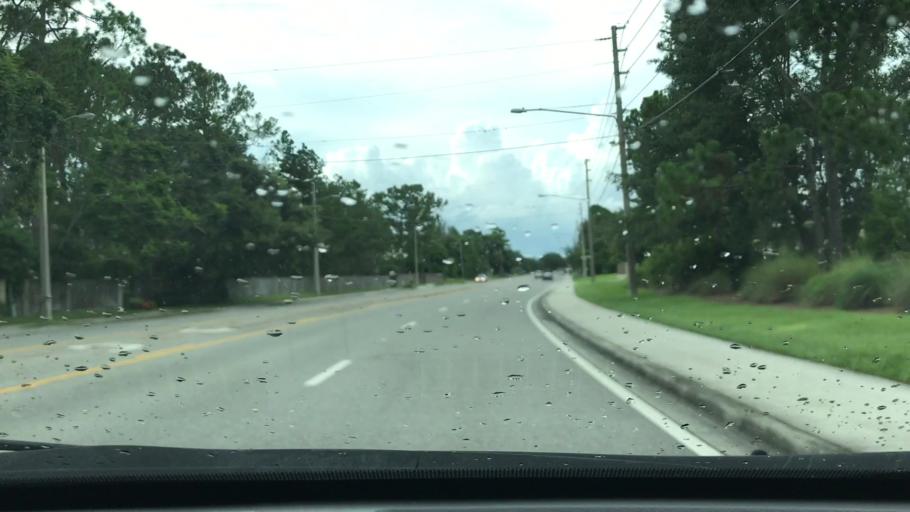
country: US
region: Florida
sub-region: Orange County
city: Williamsburg
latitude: 28.3994
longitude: -81.4746
